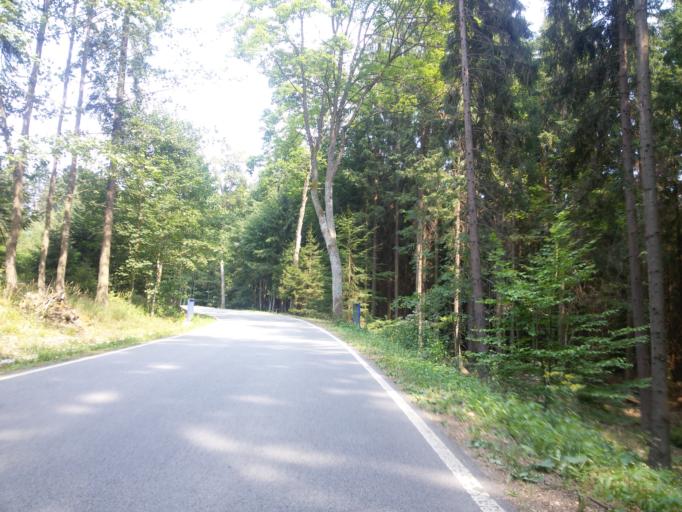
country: CZ
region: South Moravian
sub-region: Okres Brno-Venkov
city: Lomnice
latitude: 49.4616
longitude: 16.4496
